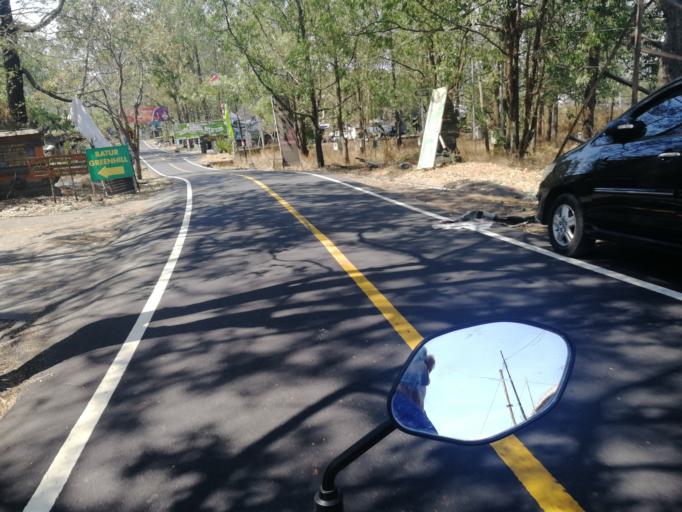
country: ID
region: Bali
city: Banjar Trunyan
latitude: -8.2528
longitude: 115.3969
